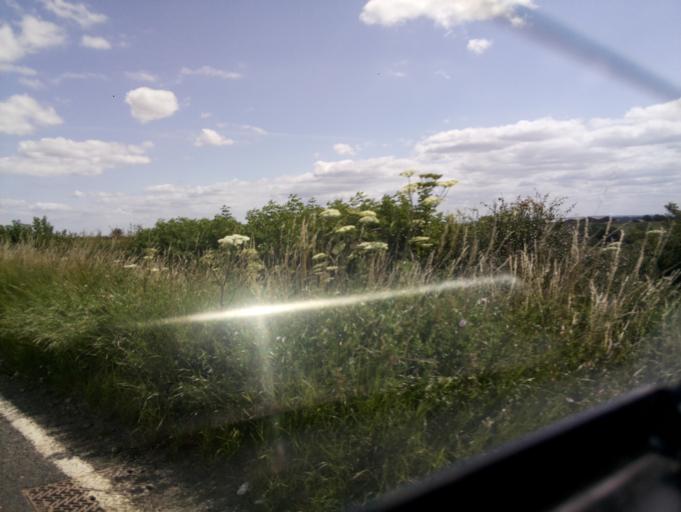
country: GB
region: England
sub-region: Buckinghamshire
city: Winslow
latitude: 51.8912
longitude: -0.8344
